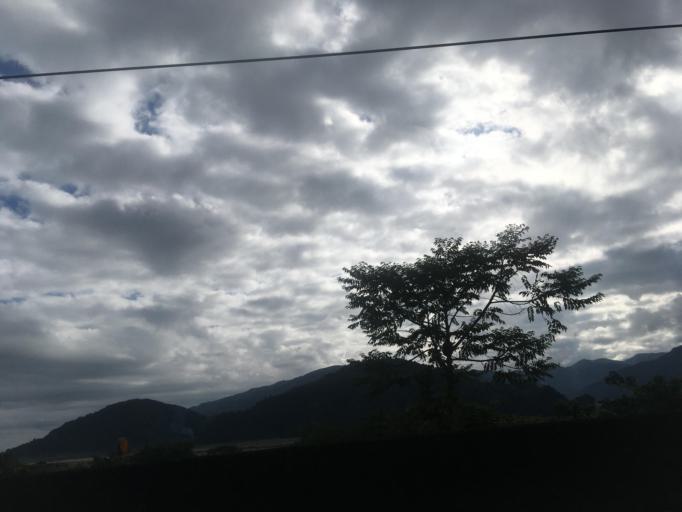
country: TW
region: Taiwan
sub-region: Yilan
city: Yilan
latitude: 24.6591
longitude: 121.5872
